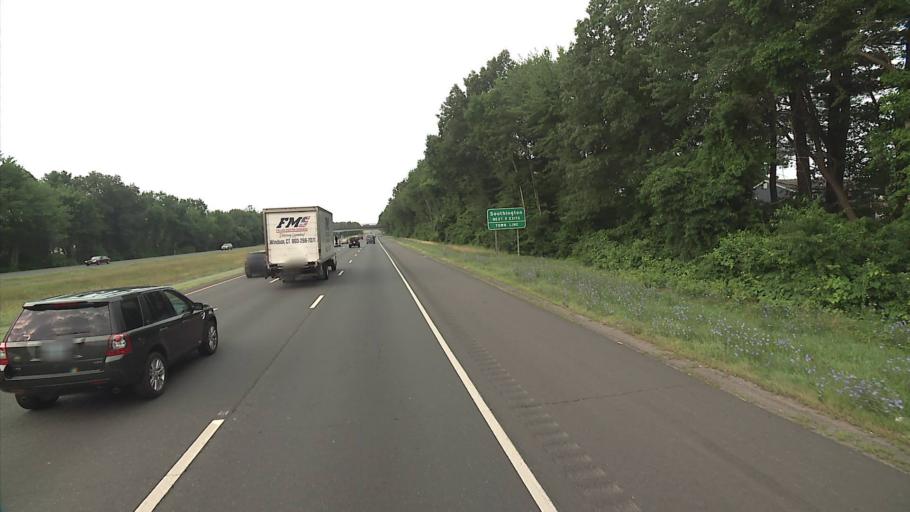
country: US
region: Connecticut
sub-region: Hartford County
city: Plainville
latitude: 41.6526
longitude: -72.8556
